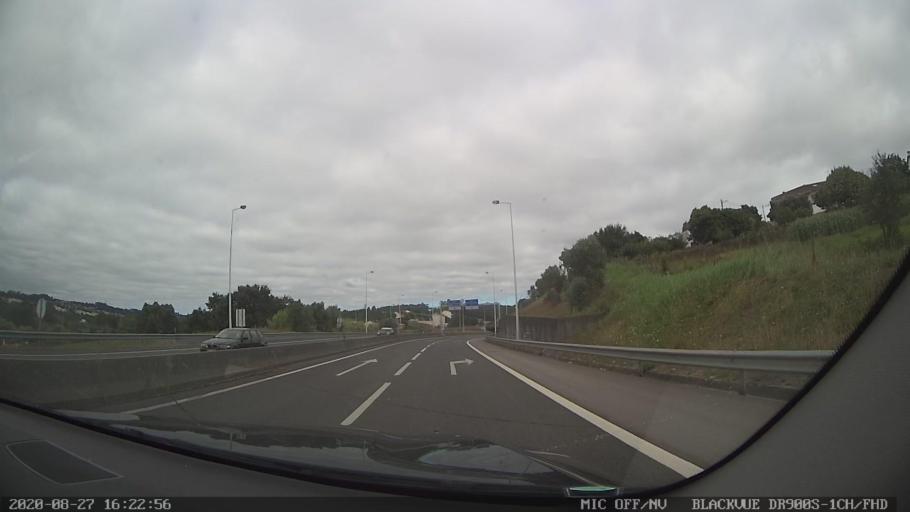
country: PT
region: Leiria
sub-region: Leiria
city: Leiria
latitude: 39.7461
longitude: -8.7772
